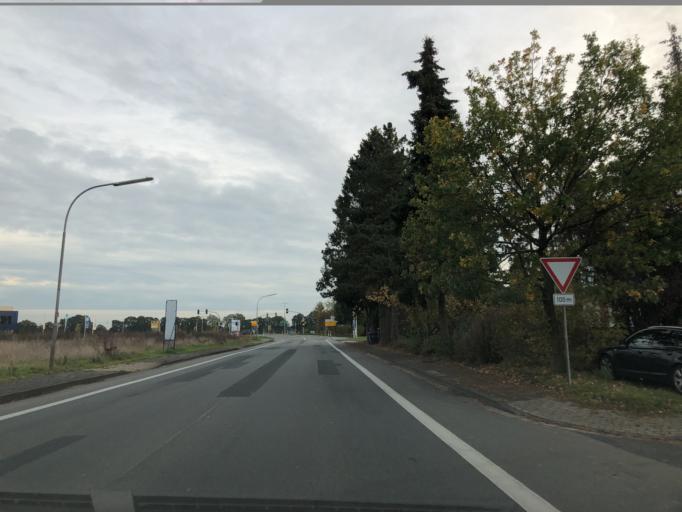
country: DE
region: Lower Saxony
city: Lehe
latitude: 53.0407
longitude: 7.3254
